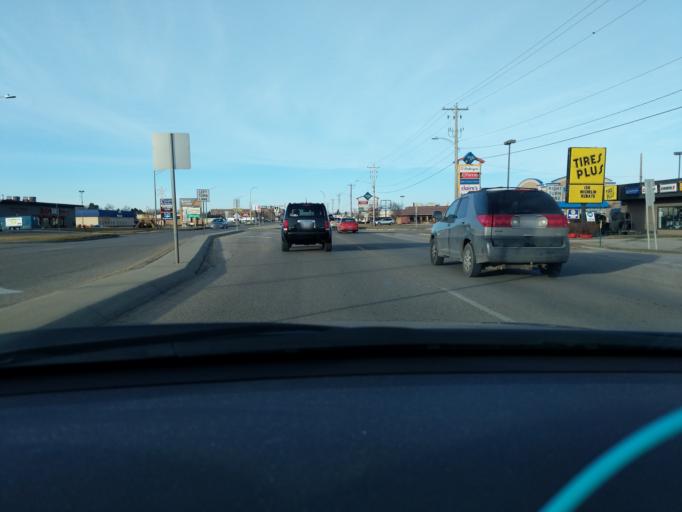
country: US
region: Minnesota
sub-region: Kandiyohi County
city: Willmar
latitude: 45.1040
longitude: -95.0426
